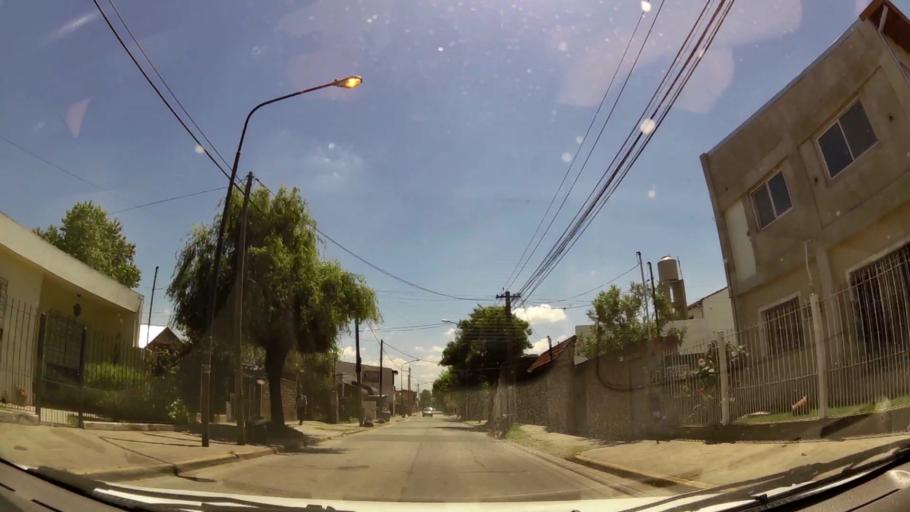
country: AR
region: Buenos Aires
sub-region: Partido de Merlo
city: Merlo
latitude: -34.6627
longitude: -58.7138
